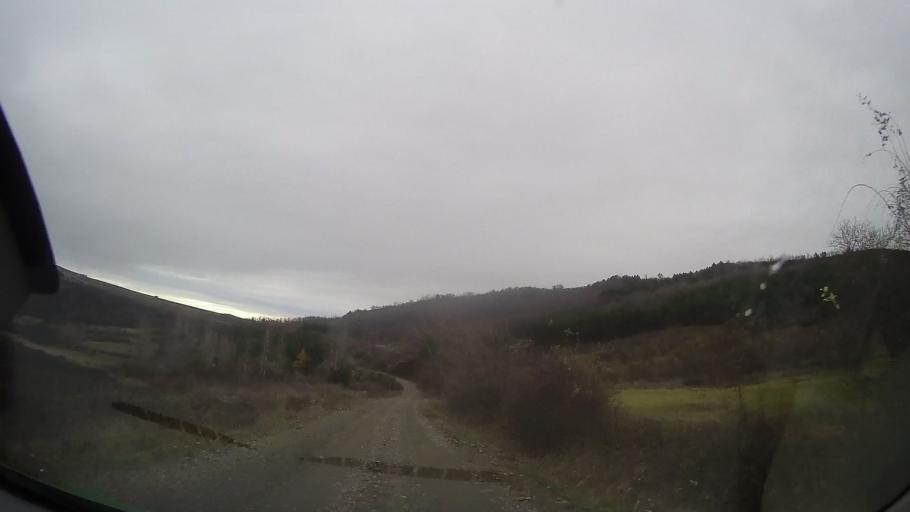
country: RO
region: Mures
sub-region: Comuna Bala
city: Bala
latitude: 46.6787
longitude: 24.4859
